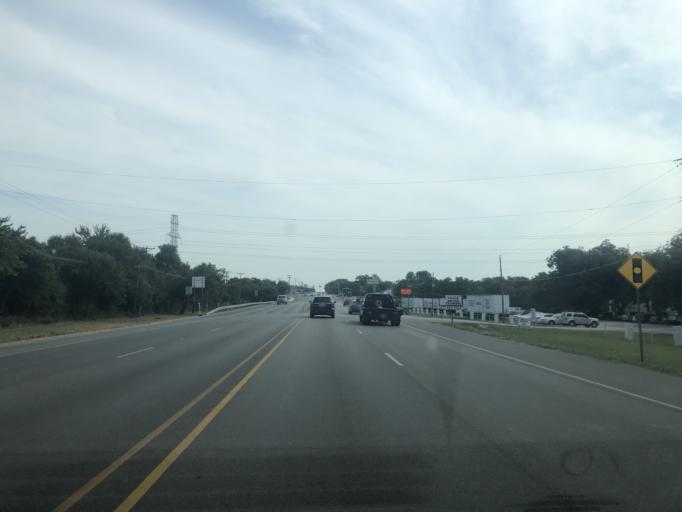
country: US
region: Texas
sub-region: Tarrant County
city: Benbrook
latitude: 32.6972
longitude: -97.4540
